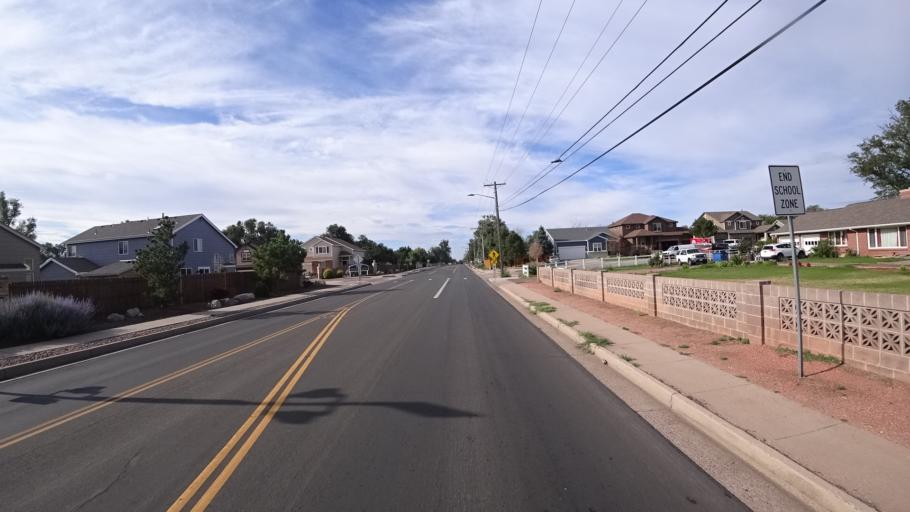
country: US
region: Colorado
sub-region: El Paso County
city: Fountain
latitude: 38.7029
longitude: -104.6969
